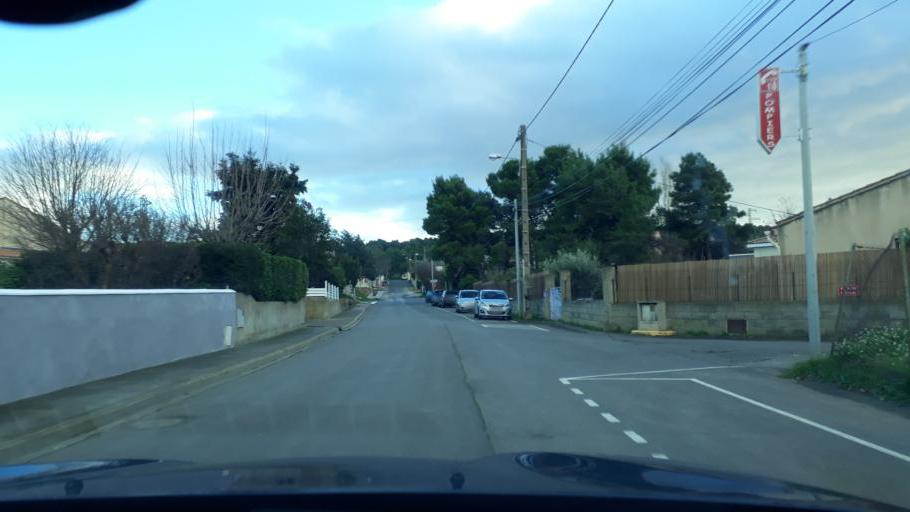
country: FR
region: Languedoc-Roussillon
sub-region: Departement de l'Herault
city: Nissan-lez-Enserune
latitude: 43.2857
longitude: 3.1326
